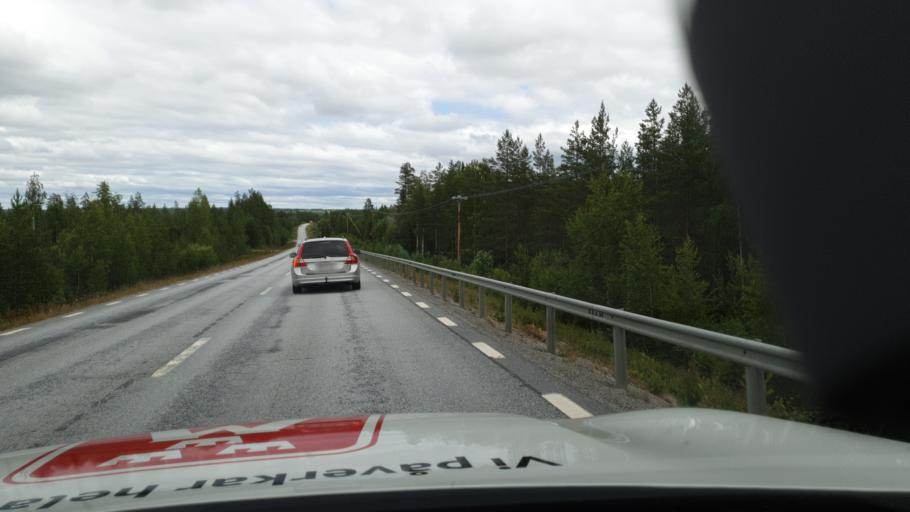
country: SE
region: Vaesterbotten
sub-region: Bjurholms Kommun
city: Bjurholm
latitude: 63.9329
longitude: 19.3785
